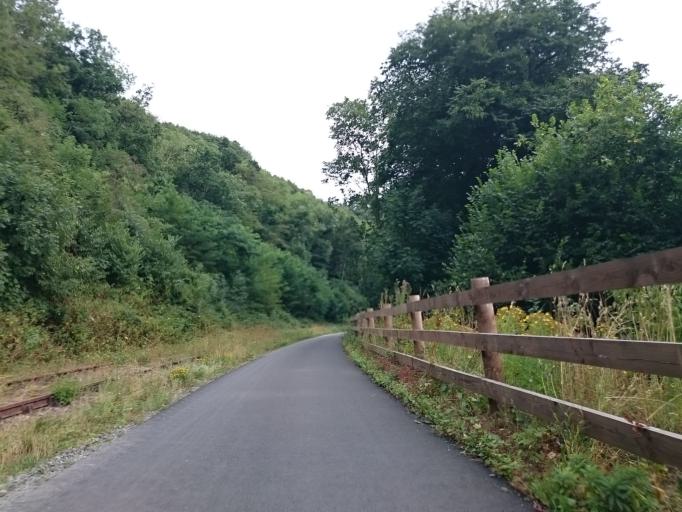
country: FR
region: Lower Normandy
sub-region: Departement du Calvados
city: Thury-Harcourt
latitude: 49.0046
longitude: -0.4652
